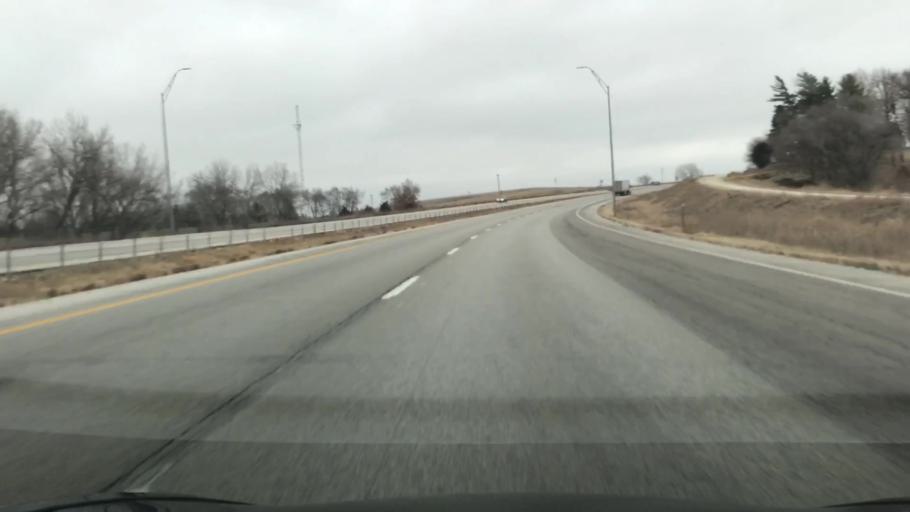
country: US
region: Iowa
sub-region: Madison County
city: Earlham
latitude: 41.5160
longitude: -94.1929
